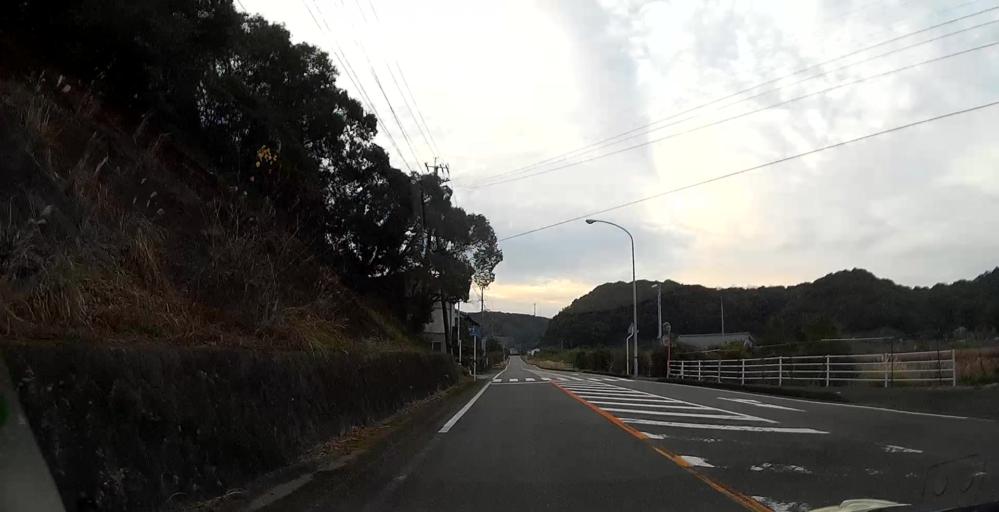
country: JP
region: Kumamoto
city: Hondo
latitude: 32.5091
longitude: 130.3809
